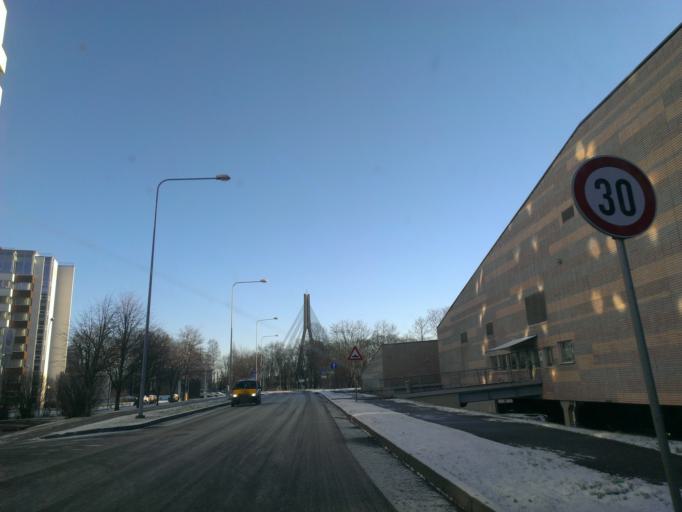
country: LV
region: Riga
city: Riga
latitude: 56.9505
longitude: 24.0822
